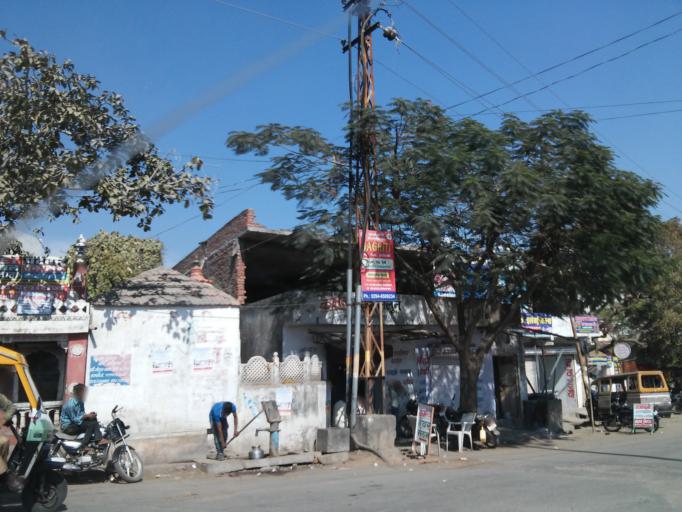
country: IN
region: Rajasthan
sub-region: Udaipur
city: Udaipur
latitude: 24.5836
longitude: 73.6518
